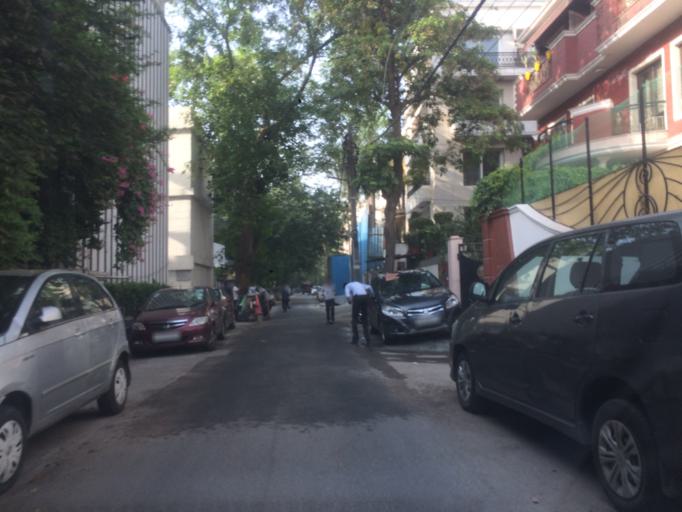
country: IN
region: NCT
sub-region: New Delhi
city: New Delhi
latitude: 28.5533
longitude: 77.2328
